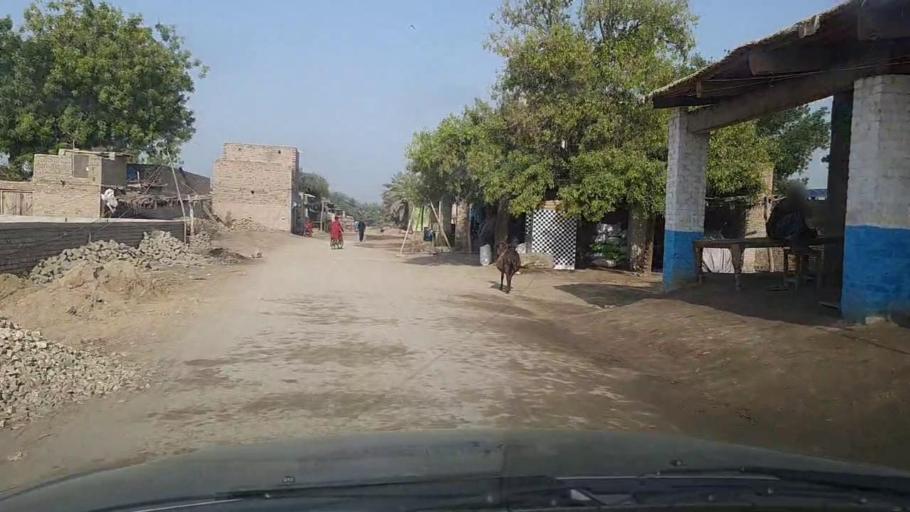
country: PK
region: Sindh
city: Pir jo Goth
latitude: 27.5568
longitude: 68.5498
